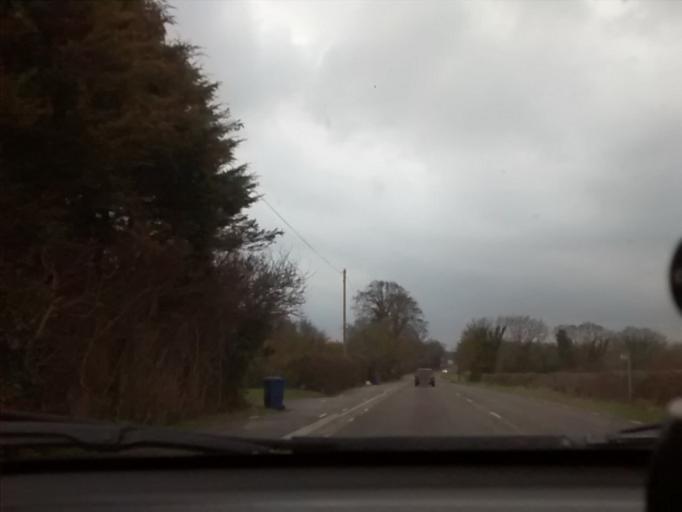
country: GB
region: England
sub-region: Cambridgeshire
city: Sawston
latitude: 52.1450
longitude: 0.1960
